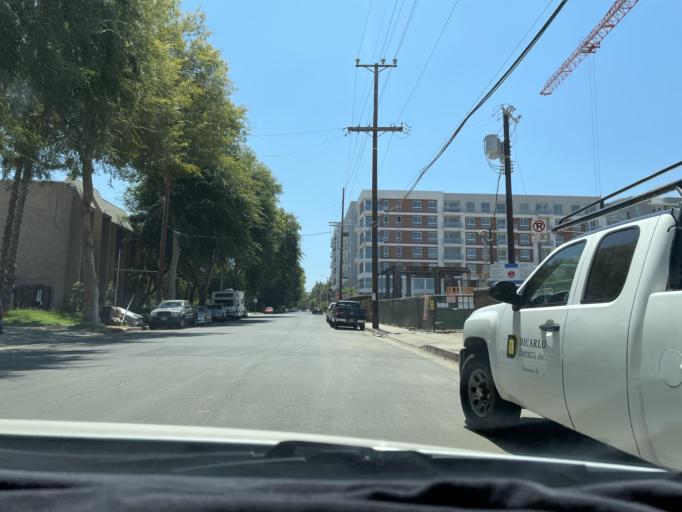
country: US
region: California
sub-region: Los Angeles County
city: Canoga Park
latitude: 34.1920
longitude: -118.5906
